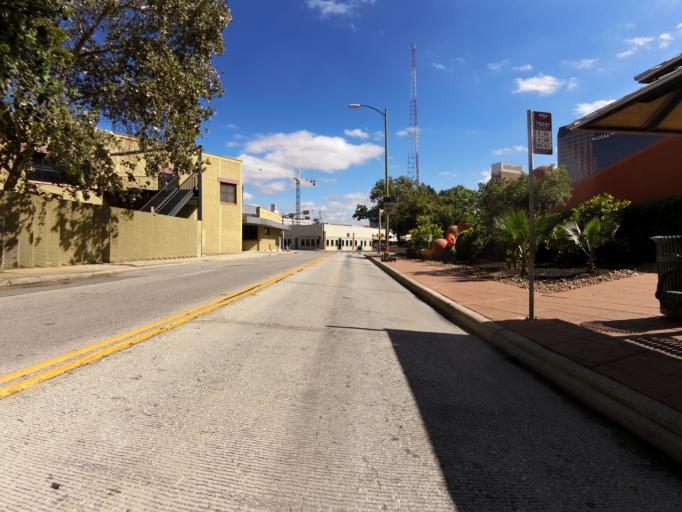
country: US
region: Texas
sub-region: Bexar County
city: San Antonio
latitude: 29.4325
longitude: -98.4922
